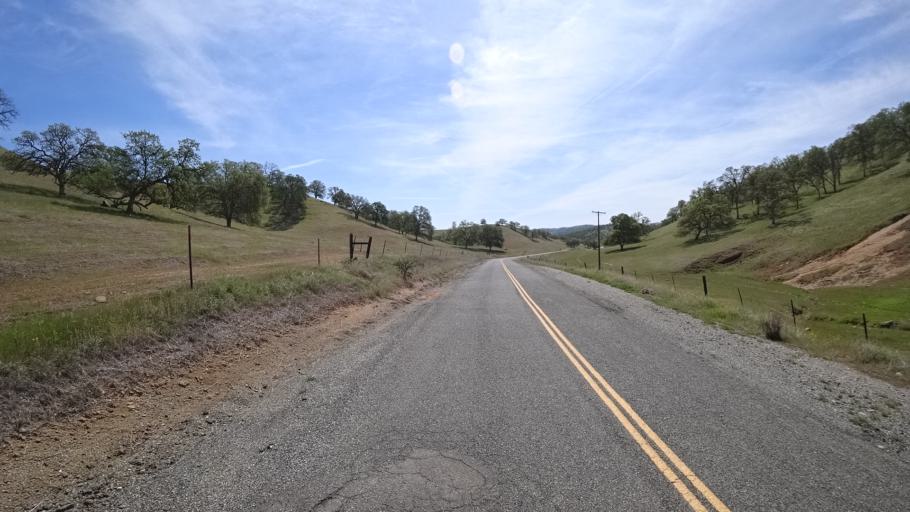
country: US
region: California
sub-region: Glenn County
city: Willows
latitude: 39.5641
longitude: -122.4399
